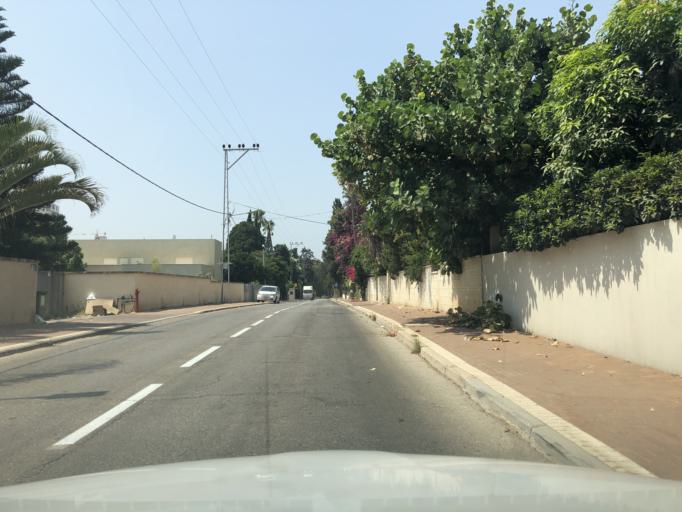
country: IL
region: Central District
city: Ganne Tiqwa
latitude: 32.0685
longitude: 34.8787
